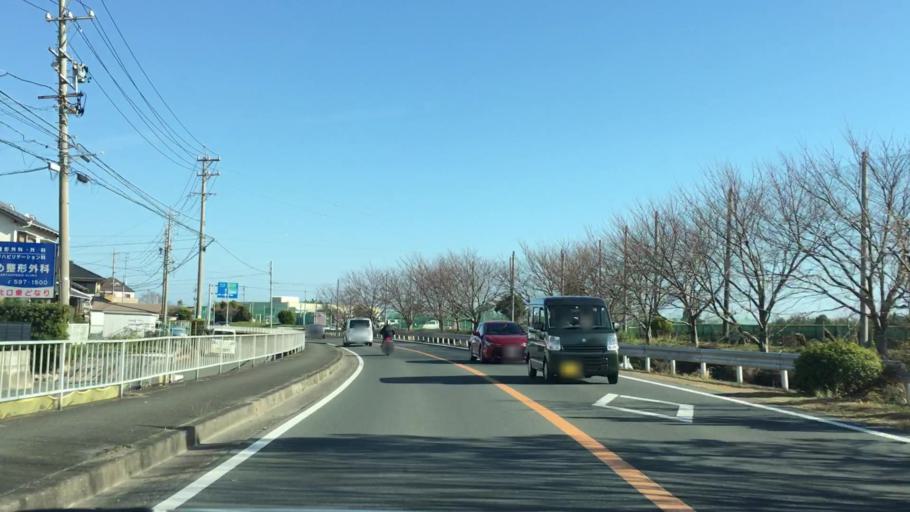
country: JP
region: Shizuoka
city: Kosai-shi
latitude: 34.6966
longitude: 137.6273
